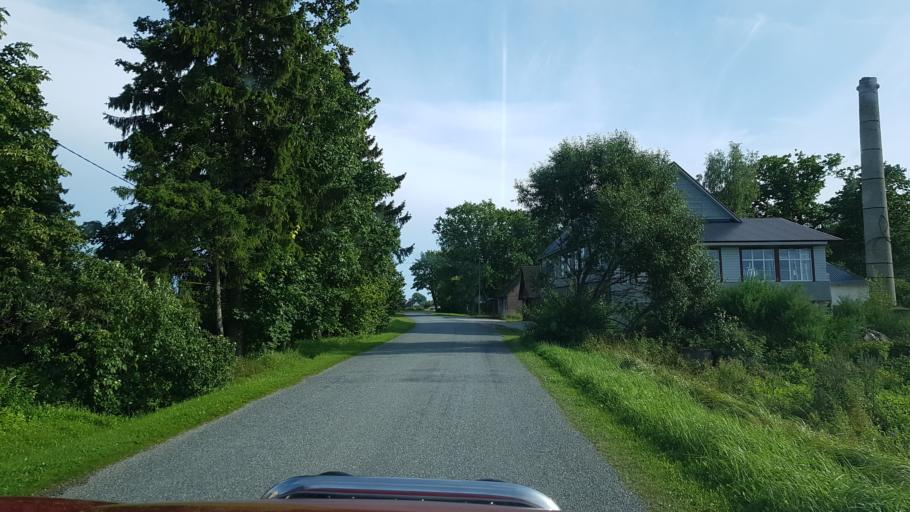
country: EE
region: Laeaene
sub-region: Lihula vald
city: Lihula
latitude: 58.4349
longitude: 24.0061
